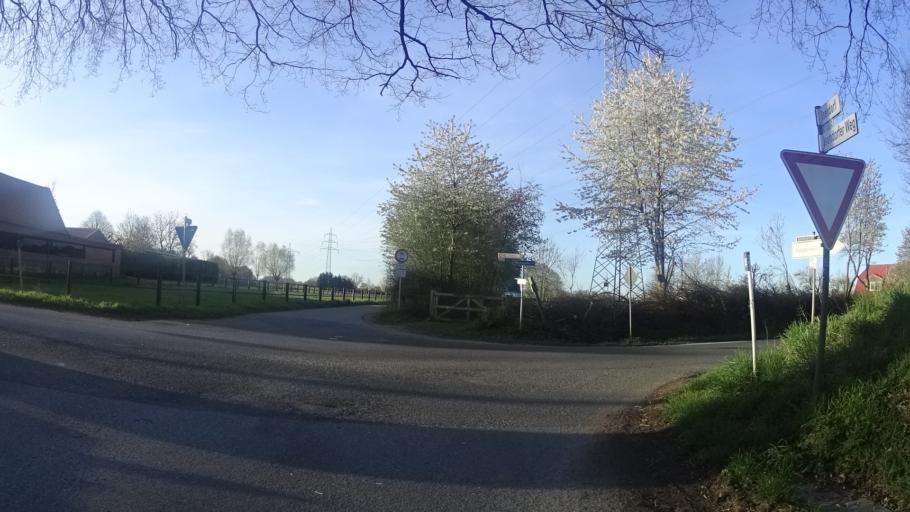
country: DE
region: North Rhine-Westphalia
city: Emsdetten
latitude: 52.2006
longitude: 7.5258
